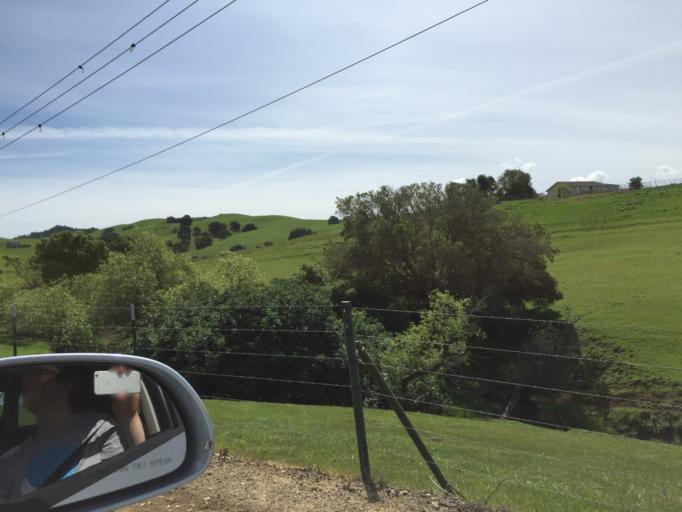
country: US
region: California
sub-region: Contra Costa County
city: Alamo
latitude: 37.8991
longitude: -121.9897
